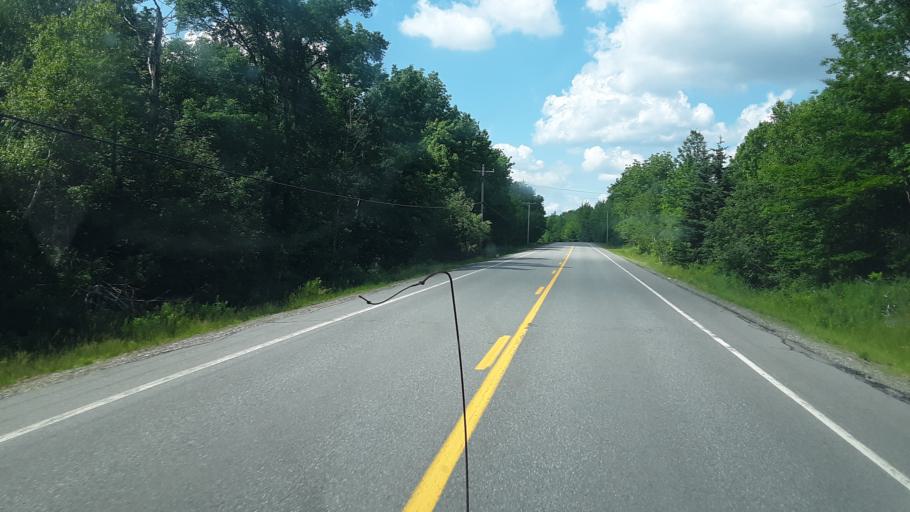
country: US
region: Maine
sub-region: Washington County
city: Machias
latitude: 45.0096
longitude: -67.5542
